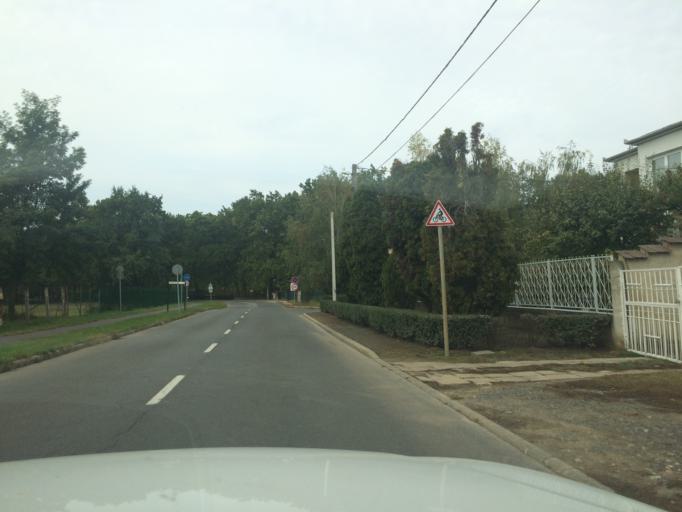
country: HU
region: Szabolcs-Szatmar-Bereg
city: Kotaj
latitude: 48.0092
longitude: 21.7308
